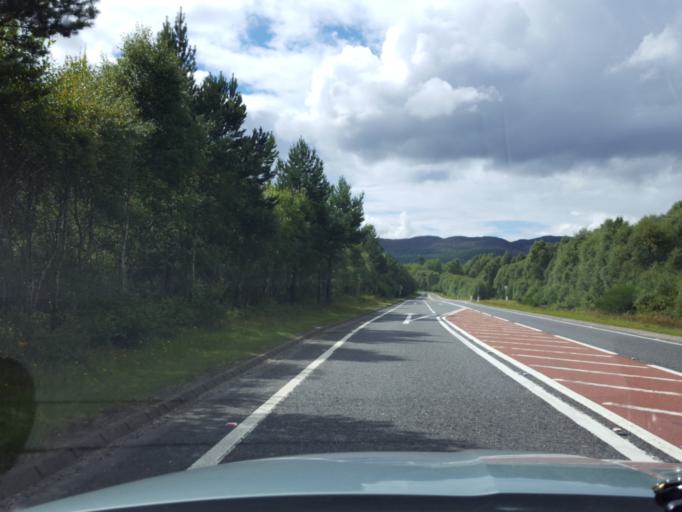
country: GB
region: Scotland
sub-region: Highland
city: Aviemore
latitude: 57.2155
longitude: -3.8181
